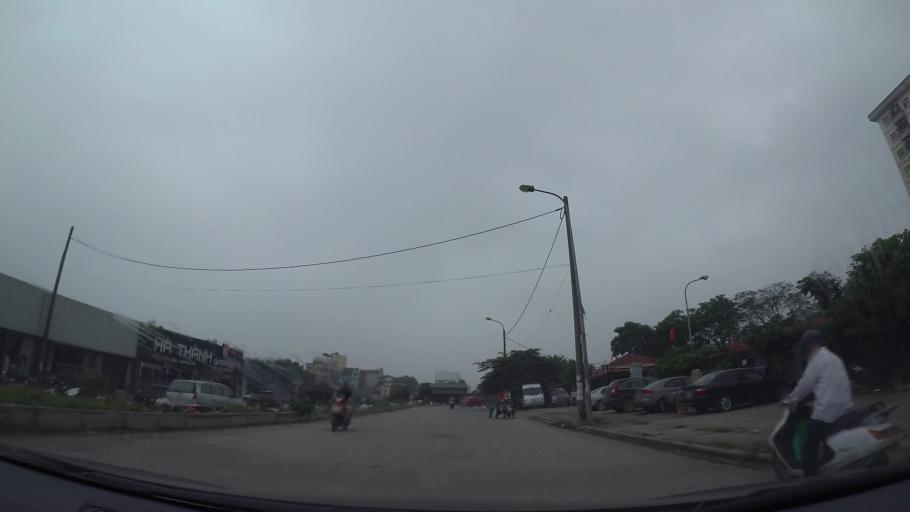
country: VN
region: Ha Noi
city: Thanh Xuan
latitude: 20.9863
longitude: 105.8273
